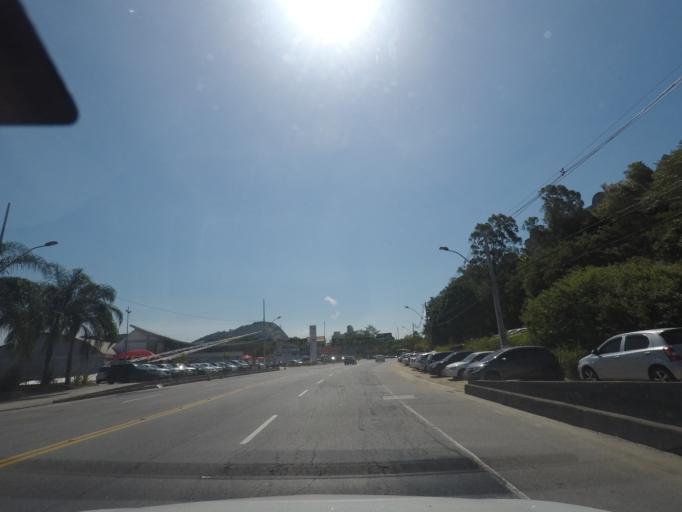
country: BR
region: Rio de Janeiro
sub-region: Niteroi
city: Niteroi
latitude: -22.9117
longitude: -43.0586
